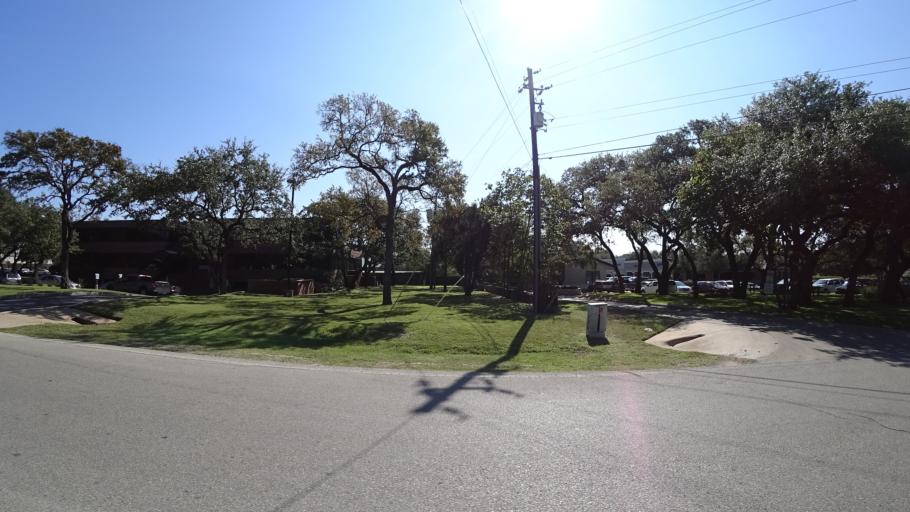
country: US
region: Texas
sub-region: Travis County
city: Rollingwood
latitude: 30.2793
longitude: -97.8080
